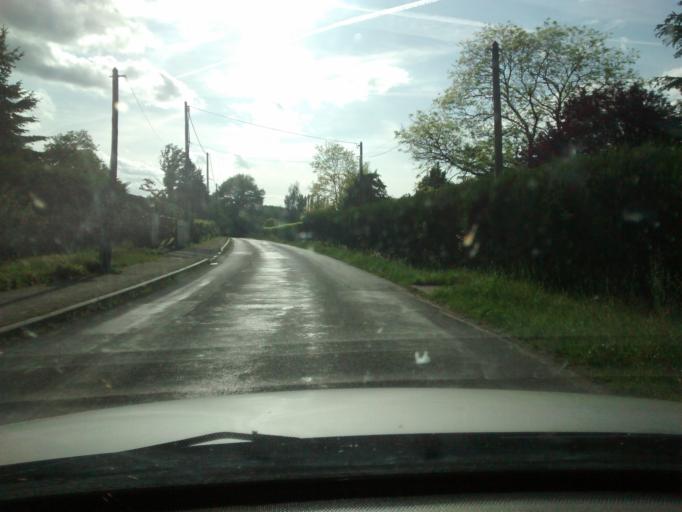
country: FR
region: Pays de la Loire
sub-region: Departement de la Sarthe
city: Brette-les-Pins
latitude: 47.9383
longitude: 0.3507
